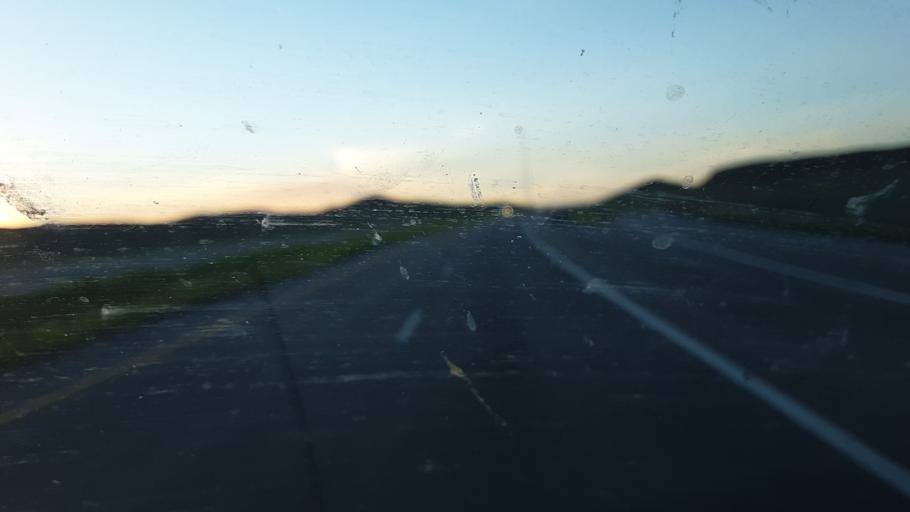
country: US
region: Wyoming
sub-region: Platte County
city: Wheatland
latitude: 41.9292
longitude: -104.9426
